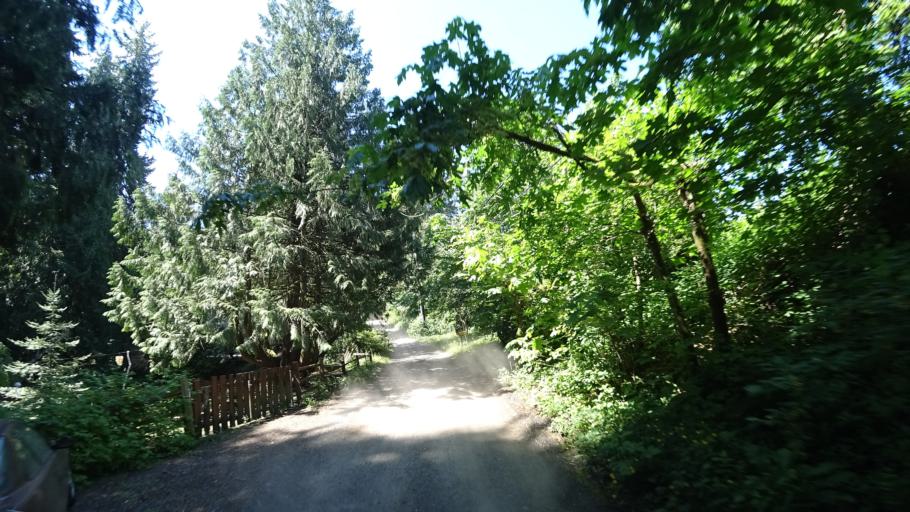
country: US
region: Oregon
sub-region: Clackamas County
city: Happy Valley
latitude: 45.4675
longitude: -122.5267
